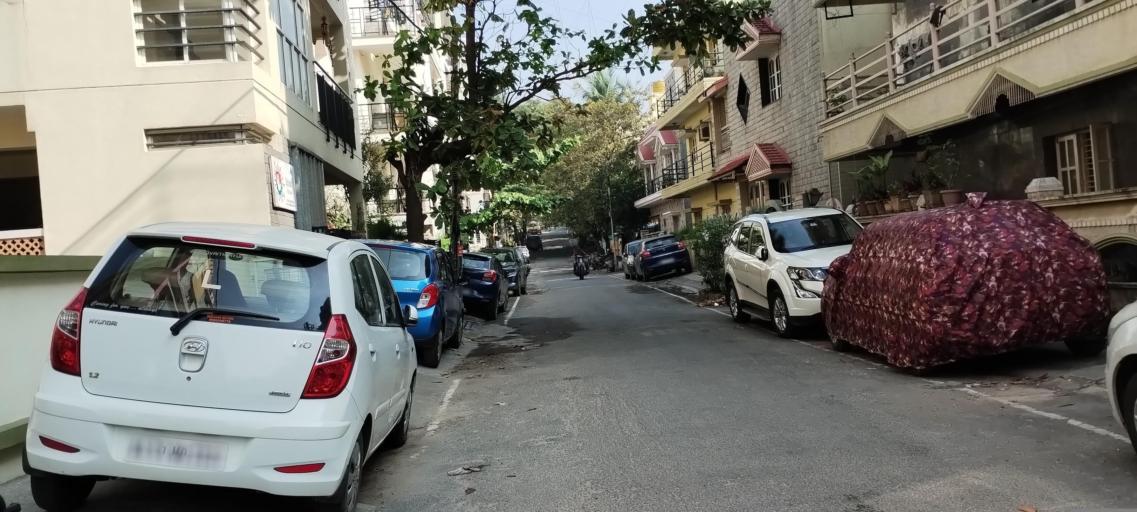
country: IN
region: Karnataka
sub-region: Bangalore Urban
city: Bangalore
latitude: 12.9356
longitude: 77.5454
